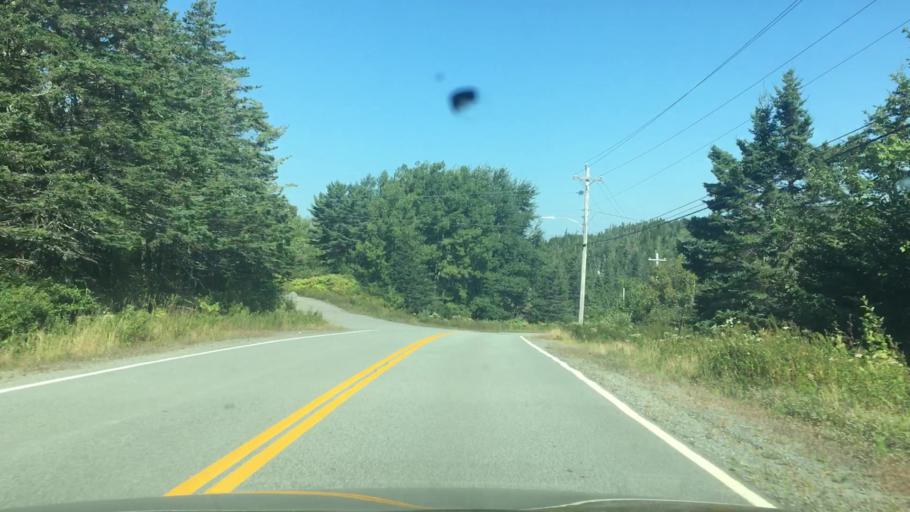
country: CA
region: Nova Scotia
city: New Glasgow
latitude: 44.8202
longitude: -62.6344
